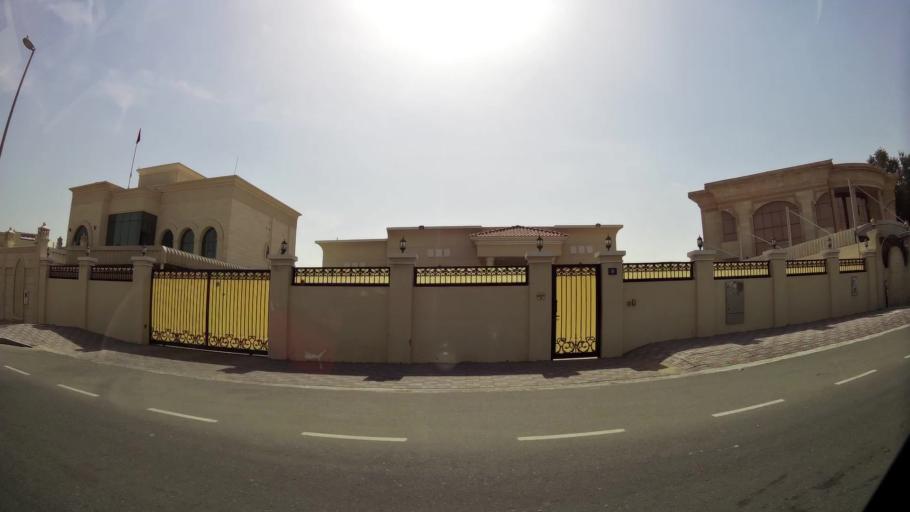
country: AE
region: Ash Shariqah
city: Sharjah
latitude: 25.2075
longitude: 55.4096
